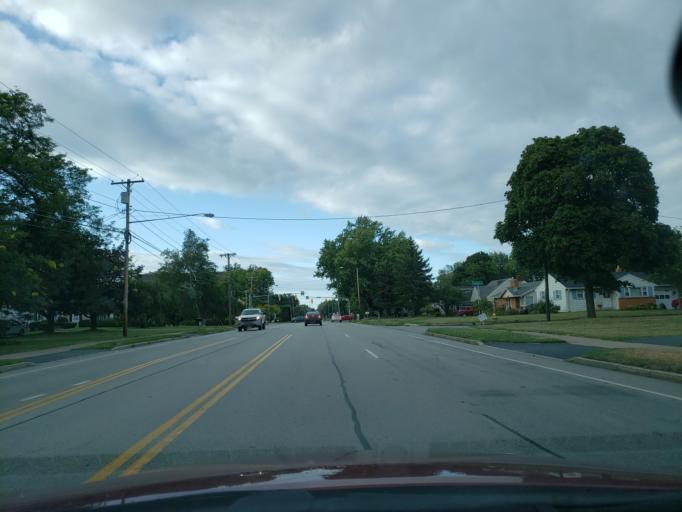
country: US
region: New York
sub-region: Monroe County
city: Greece
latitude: 43.2372
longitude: -77.6591
